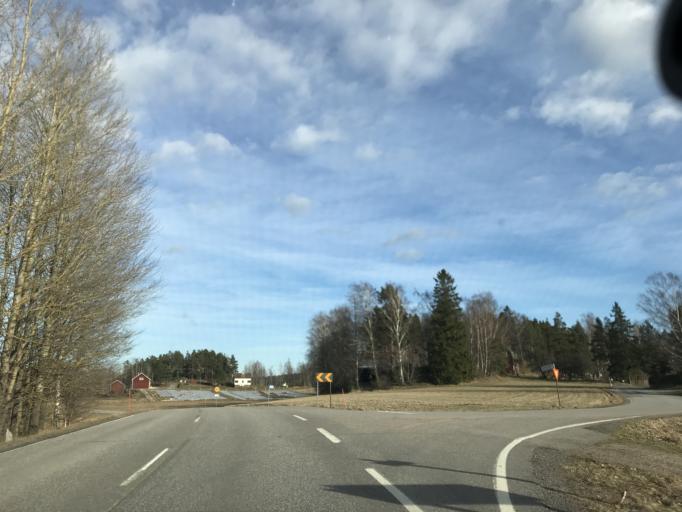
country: FI
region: Uusimaa
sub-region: Raaseporin
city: Ekenaes
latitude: 60.0752
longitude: 23.3385
